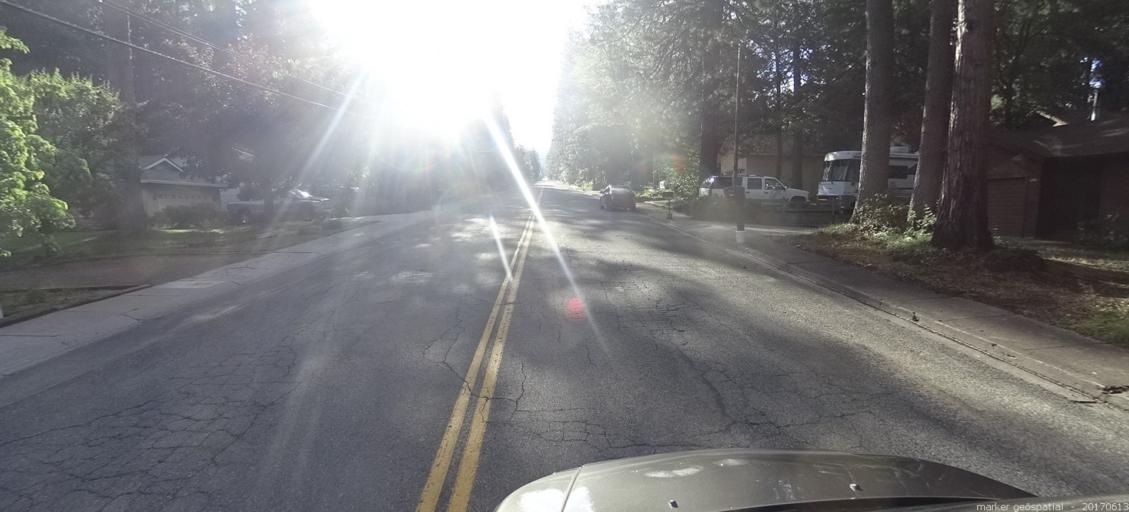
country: US
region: California
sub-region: Siskiyou County
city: Mount Shasta
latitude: 41.3122
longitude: -122.3019
